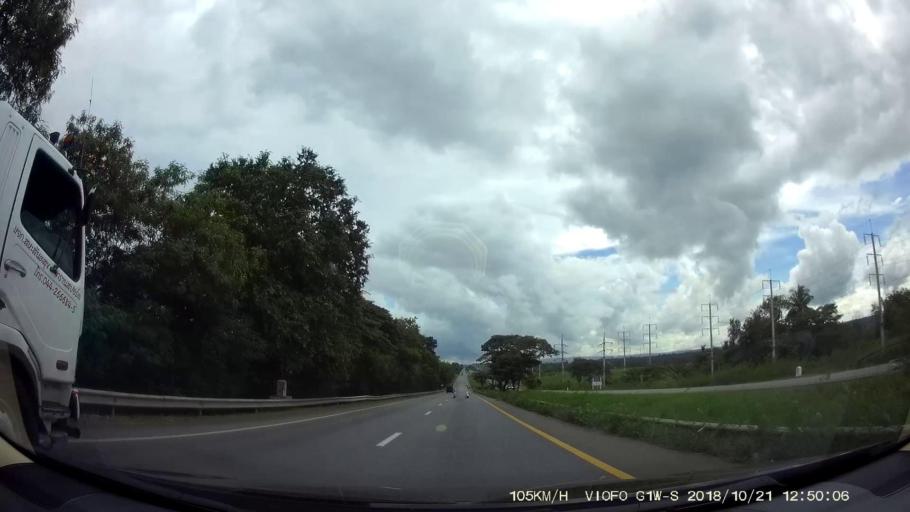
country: TH
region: Nakhon Ratchasima
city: Amphoe Sikhiu
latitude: 14.8870
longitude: 101.6881
